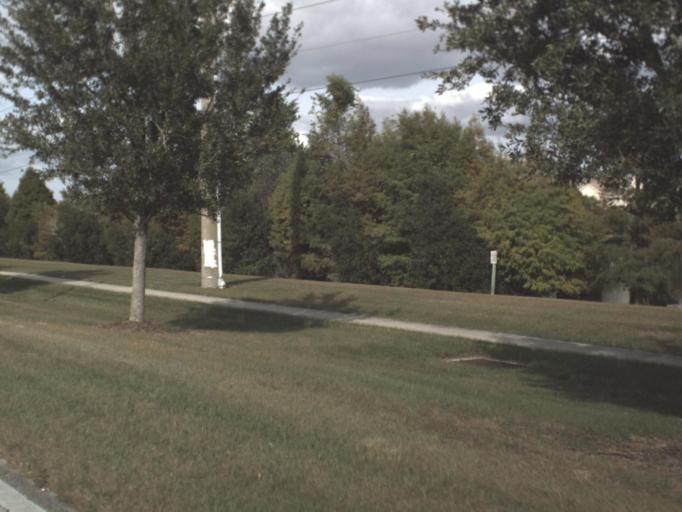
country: US
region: Florida
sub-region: Orange County
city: Hunters Creek
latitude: 28.3774
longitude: -81.4257
